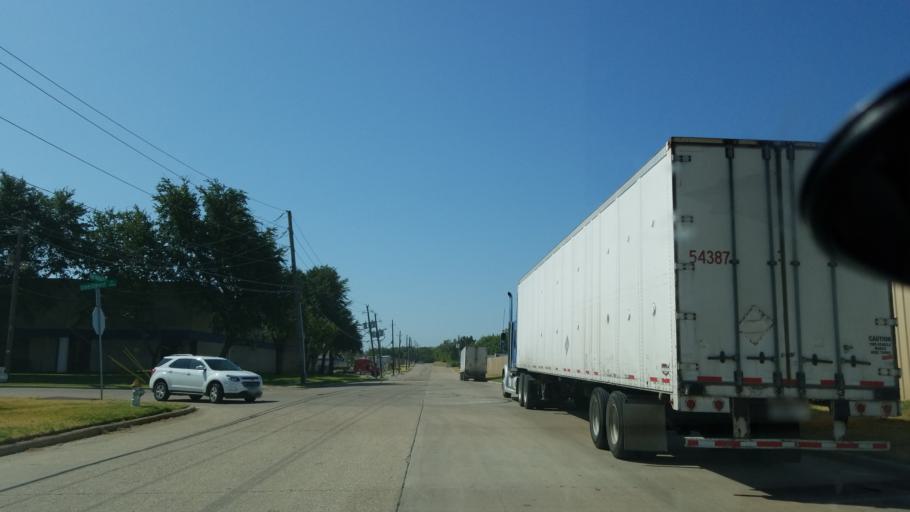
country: US
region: Texas
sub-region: Dallas County
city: Duncanville
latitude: 32.6959
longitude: -96.9162
